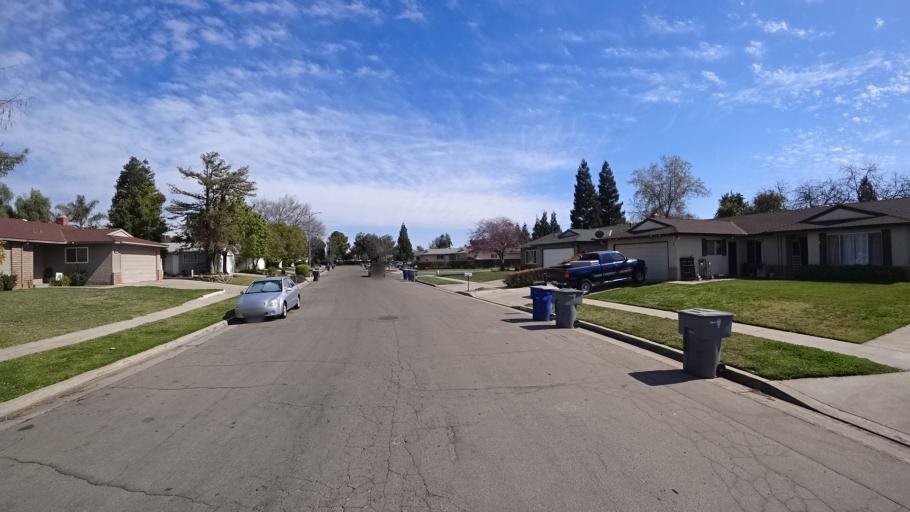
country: US
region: California
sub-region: Fresno County
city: Fresno
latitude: 36.8434
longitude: -119.8128
